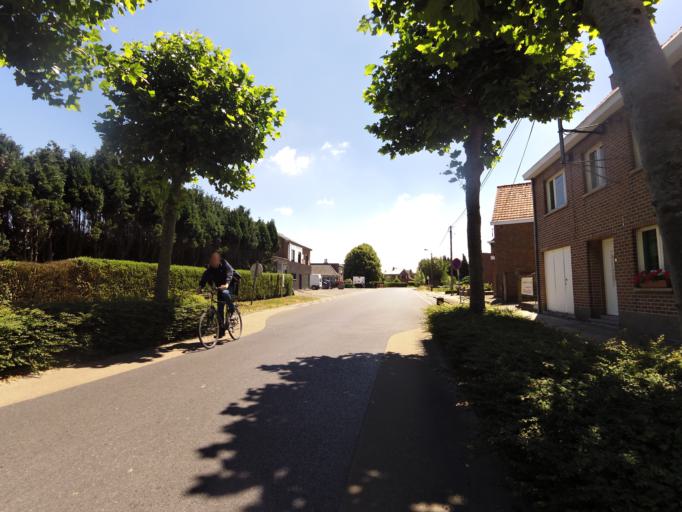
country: BE
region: Flanders
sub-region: Provincie West-Vlaanderen
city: Ichtegem
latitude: 51.1186
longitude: 3.0380
